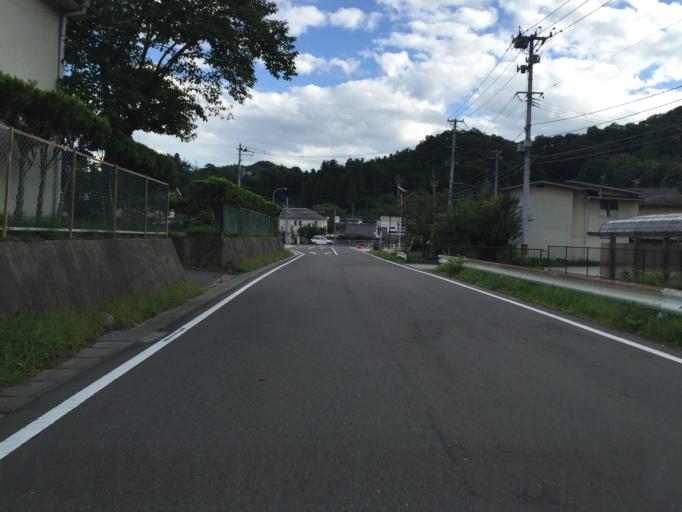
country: JP
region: Fukushima
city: Fukushima-shi
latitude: 37.6679
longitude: 140.5875
